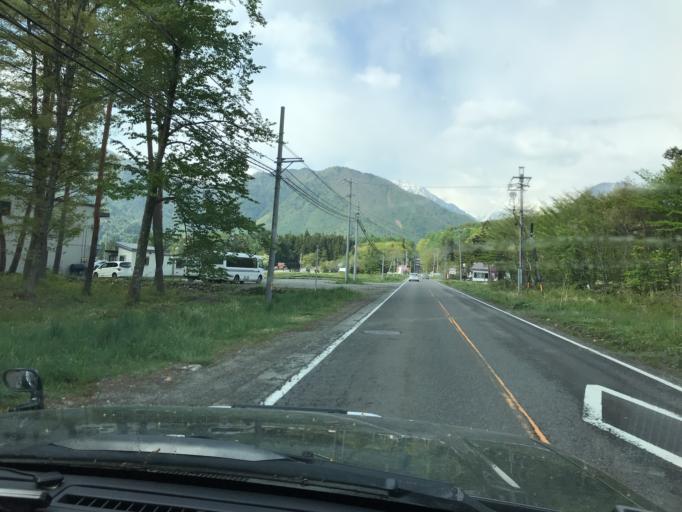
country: JP
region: Nagano
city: Omachi
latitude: 36.5263
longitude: 137.8114
